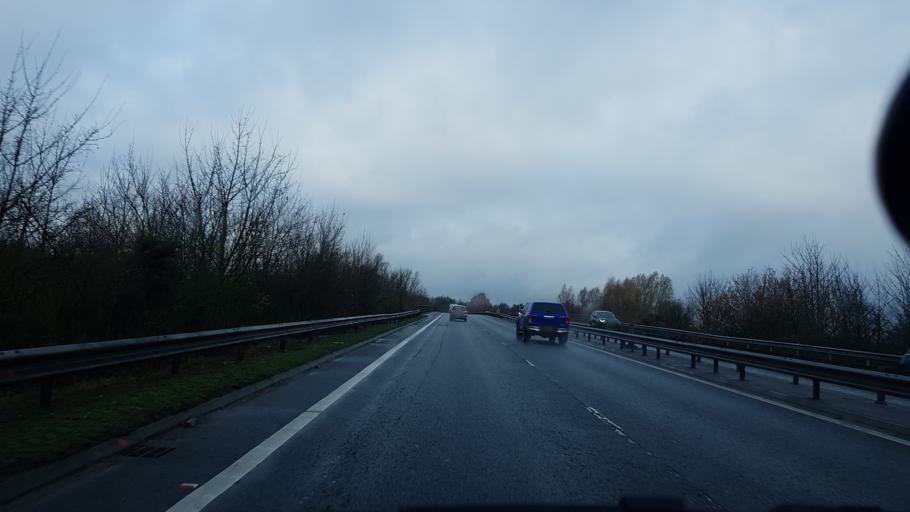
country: GB
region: England
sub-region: Bracknell Forest
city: Binfield
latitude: 51.4119
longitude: -0.7973
